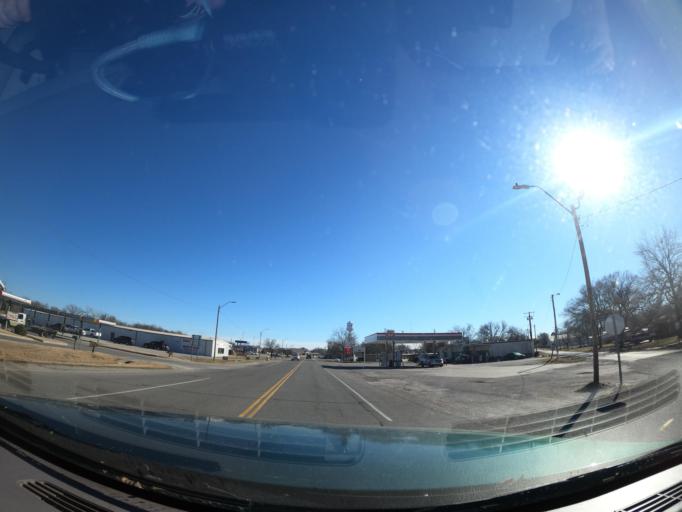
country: US
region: Oklahoma
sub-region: Muskogee County
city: Haskell
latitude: 35.8236
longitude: -95.6773
